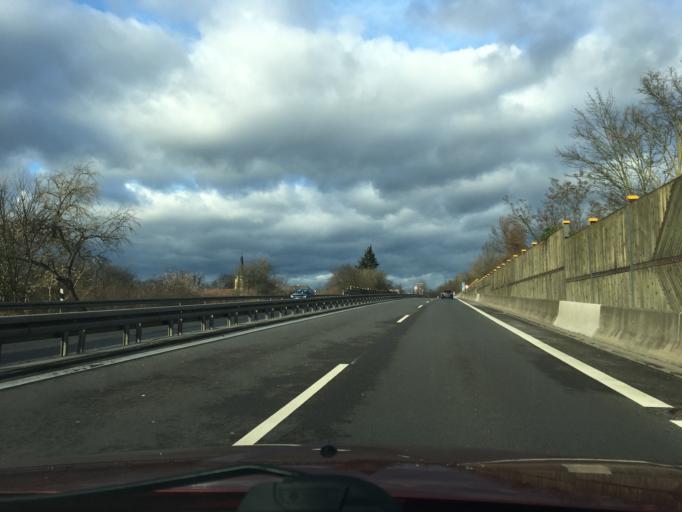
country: DE
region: Berlin
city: Bohnsdorf
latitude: 52.3980
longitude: 13.5593
